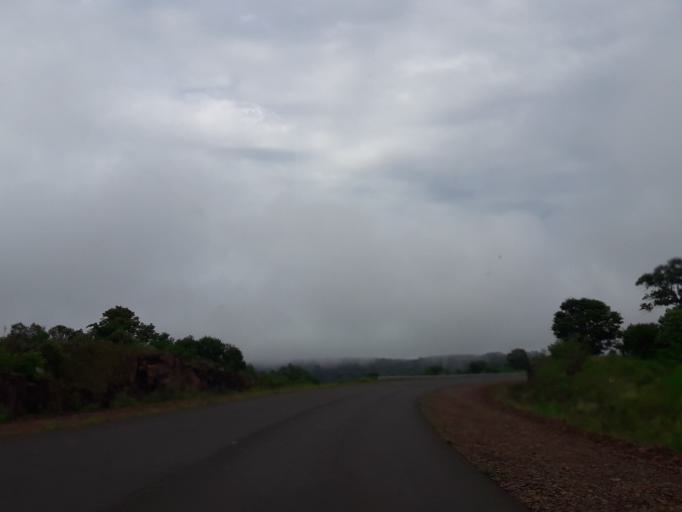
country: AR
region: Misiones
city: Bernardo de Irigoyen
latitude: -26.4195
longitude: -53.8256
